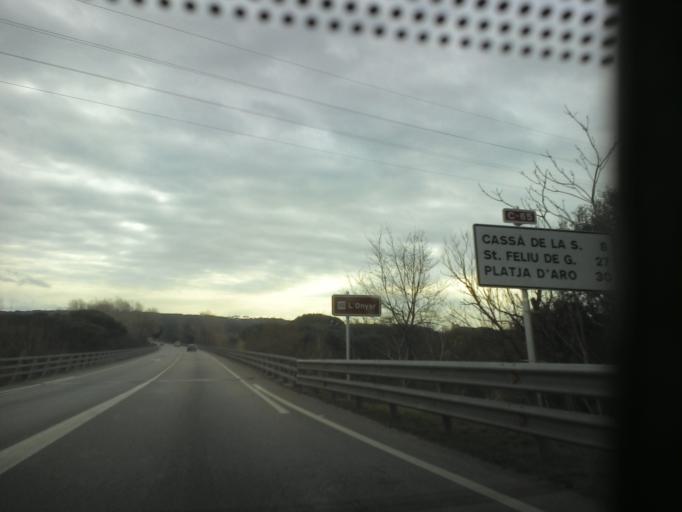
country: ES
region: Catalonia
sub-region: Provincia de Girona
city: Fornells de la Selva
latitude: 41.9404
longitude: 2.8189
